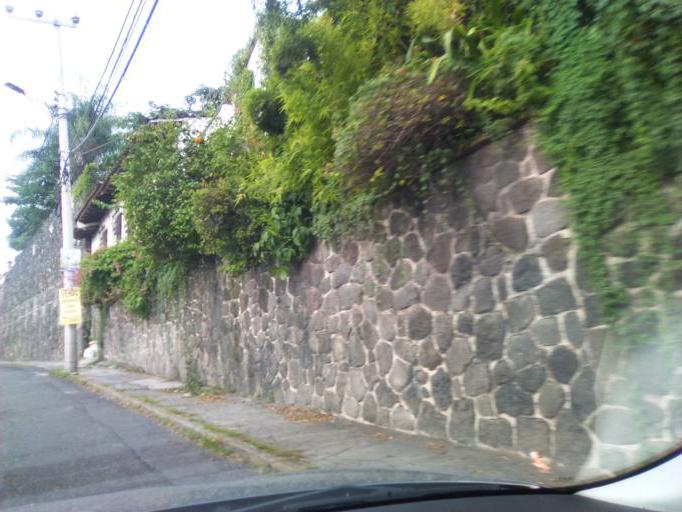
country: MX
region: Morelos
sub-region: Cuernavaca
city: Cuernavaca
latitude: 18.9132
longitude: -99.2294
